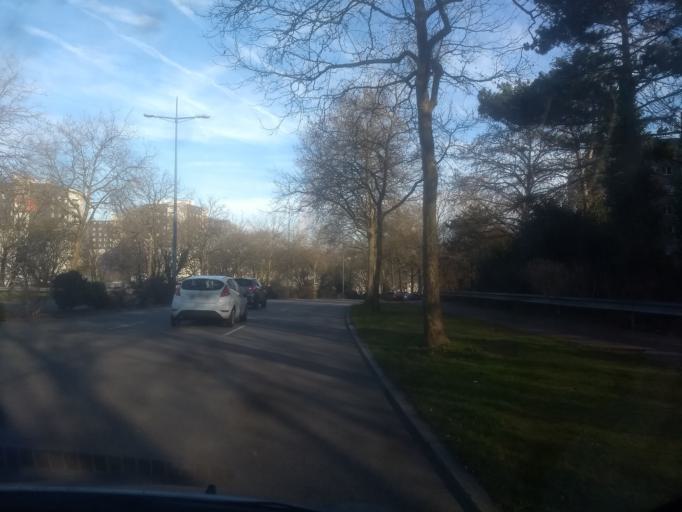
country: FR
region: Limousin
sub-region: Departement de la Haute-Vienne
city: Isle
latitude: 45.8316
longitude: 1.2252
